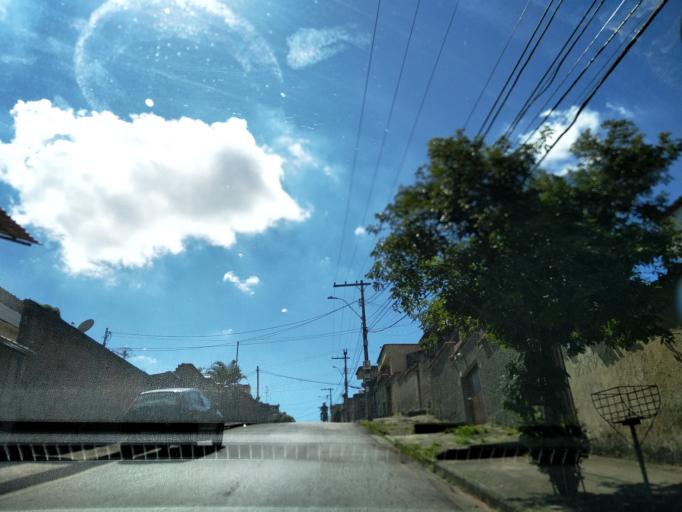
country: BR
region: Minas Gerais
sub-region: Belo Horizonte
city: Belo Horizonte
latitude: -19.8667
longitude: -43.9009
